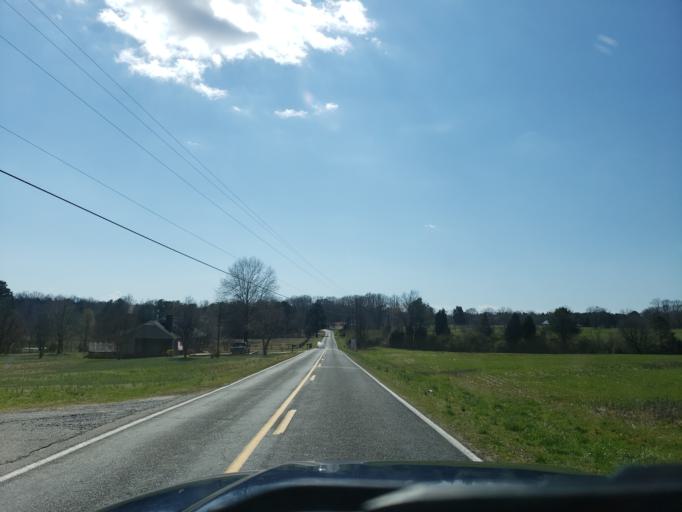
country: US
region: North Carolina
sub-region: Cleveland County
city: White Plains
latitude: 35.2327
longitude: -81.3991
